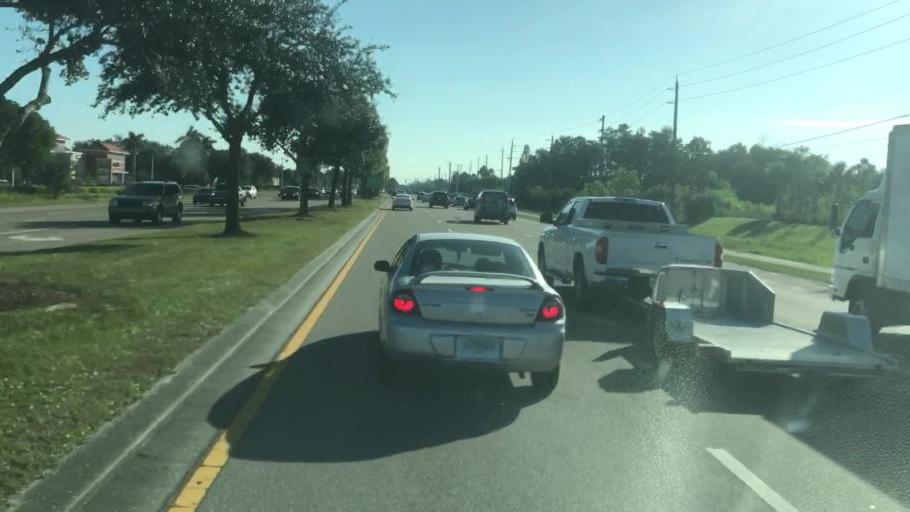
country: US
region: Florida
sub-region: Lee County
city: Villas
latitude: 26.5472
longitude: -81.8077
